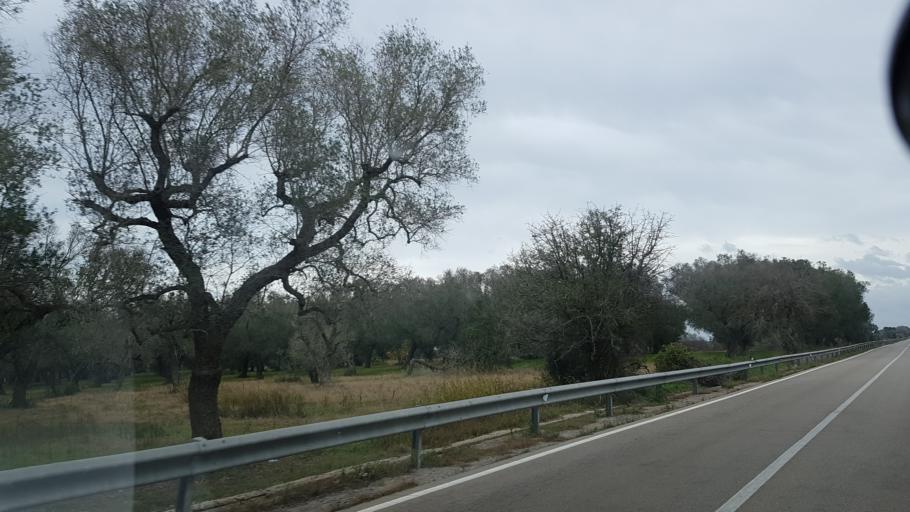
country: IT
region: Apulia
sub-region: Provincia di Brindisi
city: San Donaci
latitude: 40.4063
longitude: 17.8891
